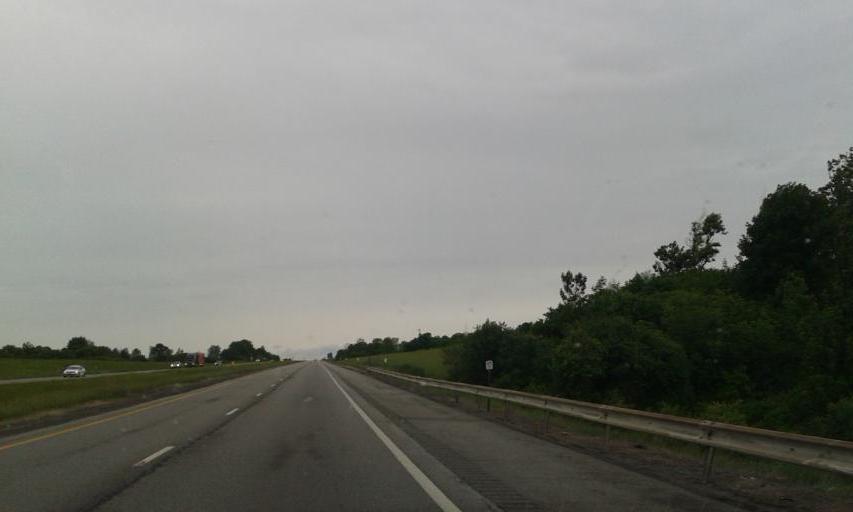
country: US
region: New York
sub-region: Genesee County
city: Bergen
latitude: 43.0287
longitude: -77.9467
